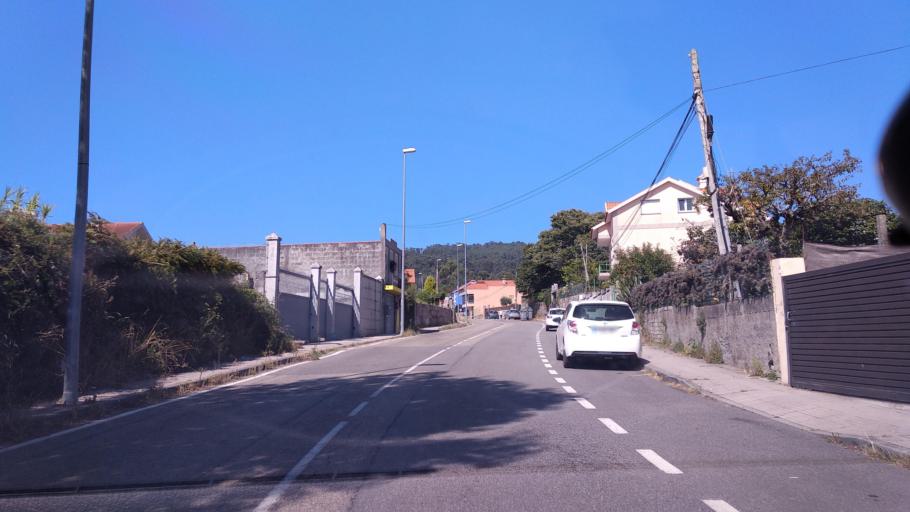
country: ES
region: Galicia
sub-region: Provincia de Pontevedra
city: Cangas
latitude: 42.2703
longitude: -8.7679
